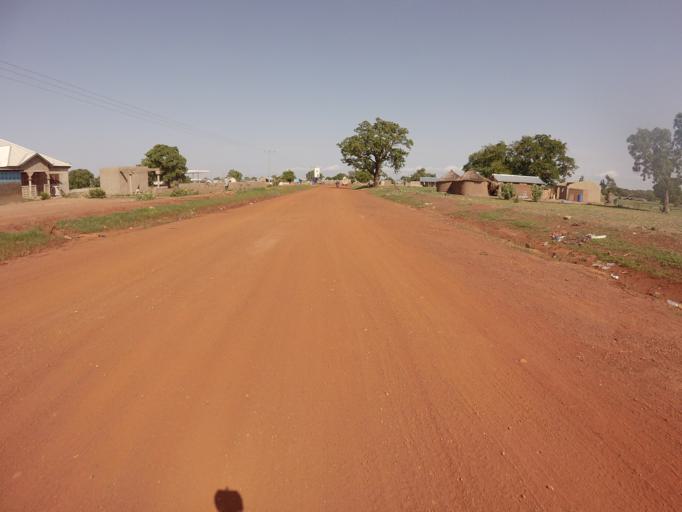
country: GH
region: Upper East
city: Bawku
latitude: 10.8316
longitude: -0.1710
